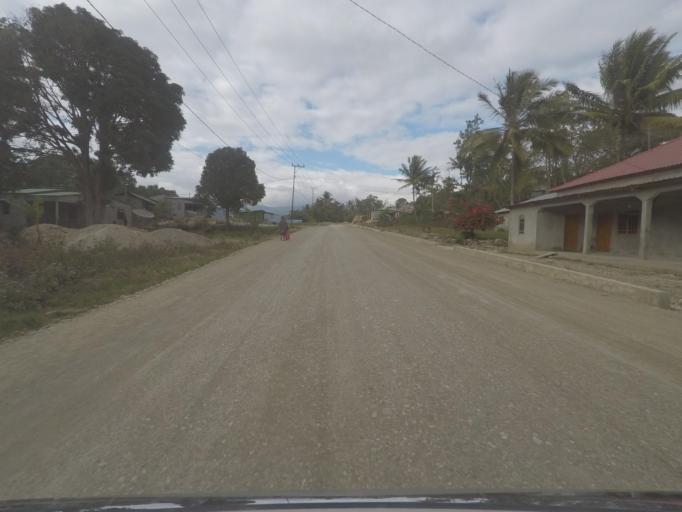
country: TL
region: Baucau
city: Venilale
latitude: -8.6174
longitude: 126.3831
